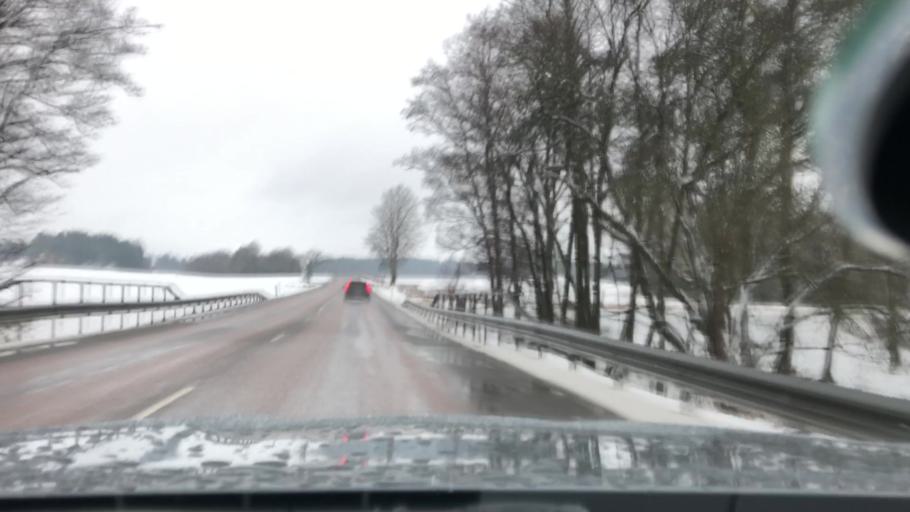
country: SE
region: Stockholm
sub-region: Sodertalje Kommun
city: Pershagen
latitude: 59.0523
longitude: 17.6095
